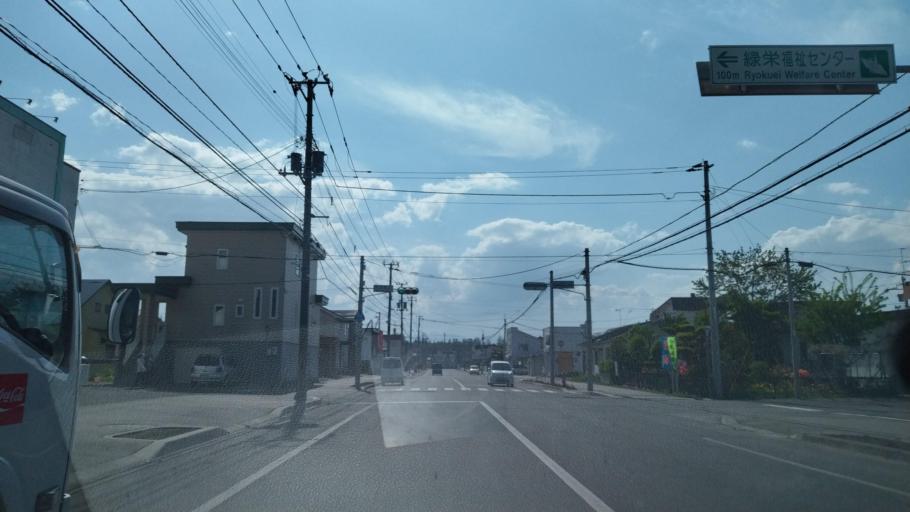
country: JP
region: Hokkaido
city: Obihiro
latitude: 42.9008
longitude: 143.1950
